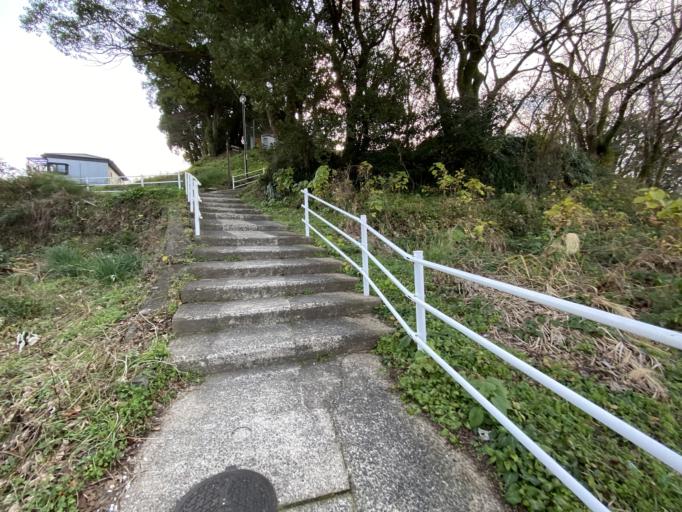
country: JP
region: Nagasaki
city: Nagasaki-shi
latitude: 32.7474
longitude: 129.8865
